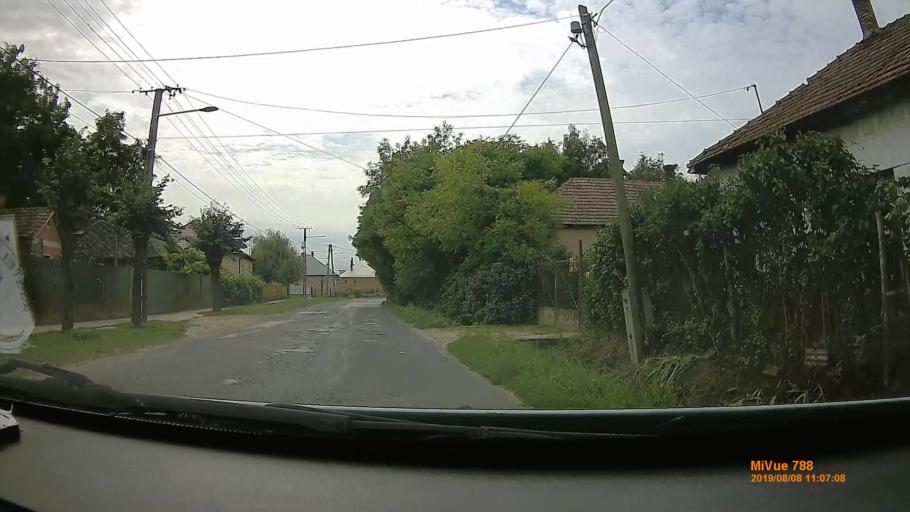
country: HU
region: Szabolcs-Szatmar-Bereg
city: Balkany
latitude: 47.7671
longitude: 21.8501
